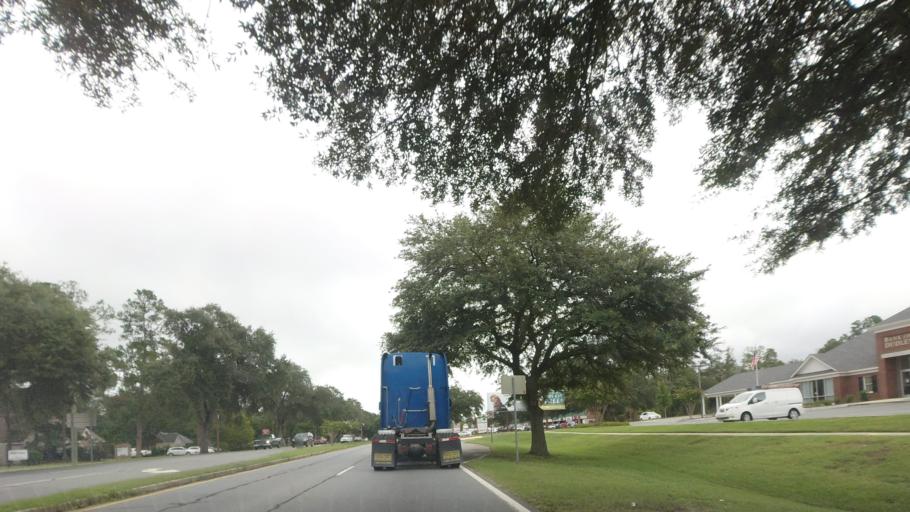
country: US
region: Georgia
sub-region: Laurens County
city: Dublin
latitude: 32.5368
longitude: -82.9341
